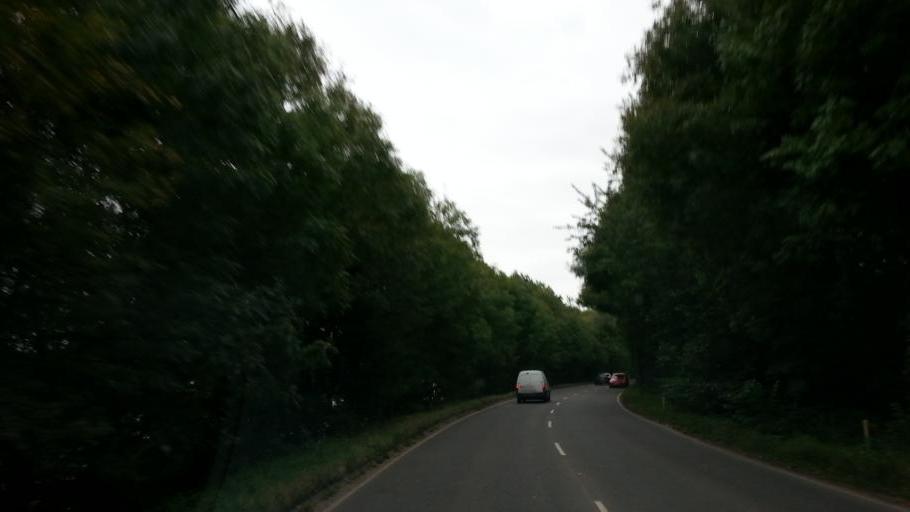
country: GB
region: England
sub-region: Cambridgeshire
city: Needingworth
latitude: 52.3304
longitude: -0.0596
